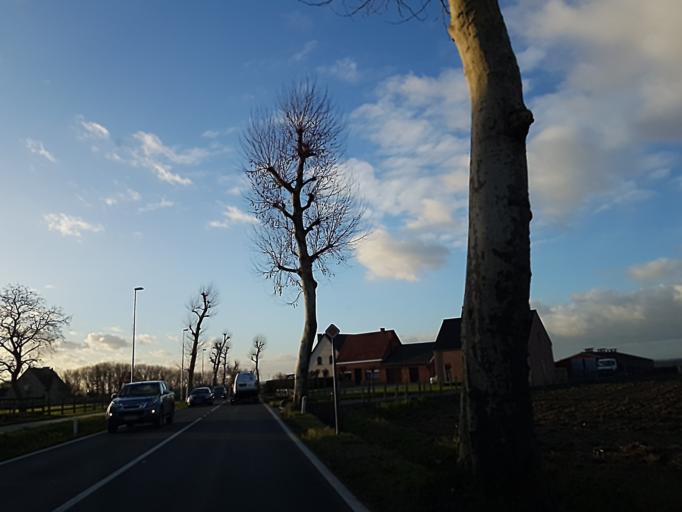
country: BE
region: Flanders
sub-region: Provincie Oost-Vlaanderen
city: Kruishoutem
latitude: 50.9076
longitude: 3.5143
